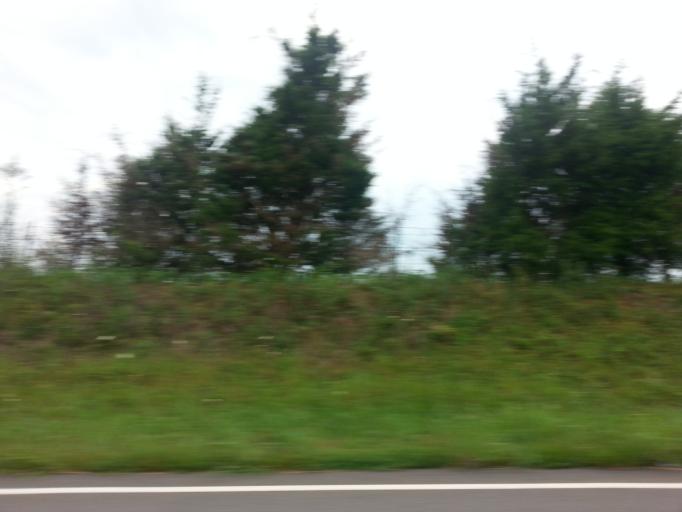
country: US
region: Tennessee
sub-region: Loudon County
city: Greenback
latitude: 35.6467
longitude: -84.1991
